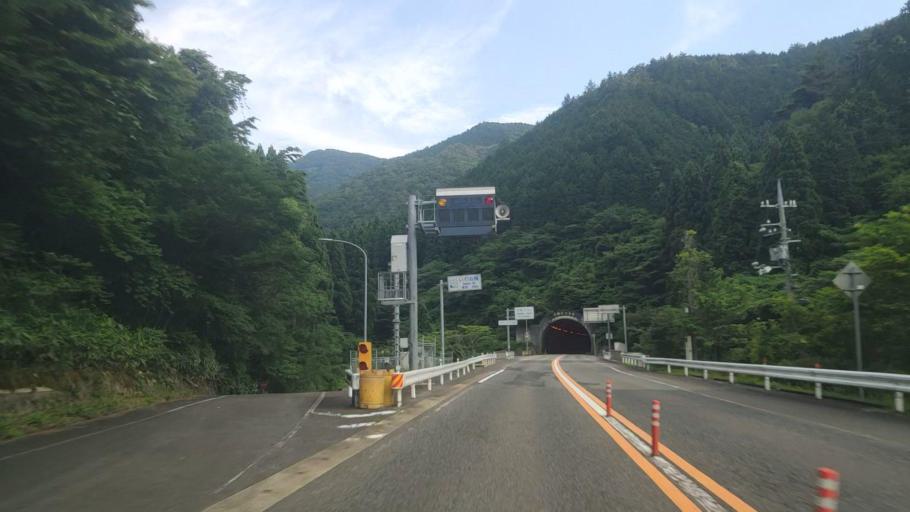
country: JP
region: Tottori
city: Kurayoshi
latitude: 35.3188
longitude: 133.7562
